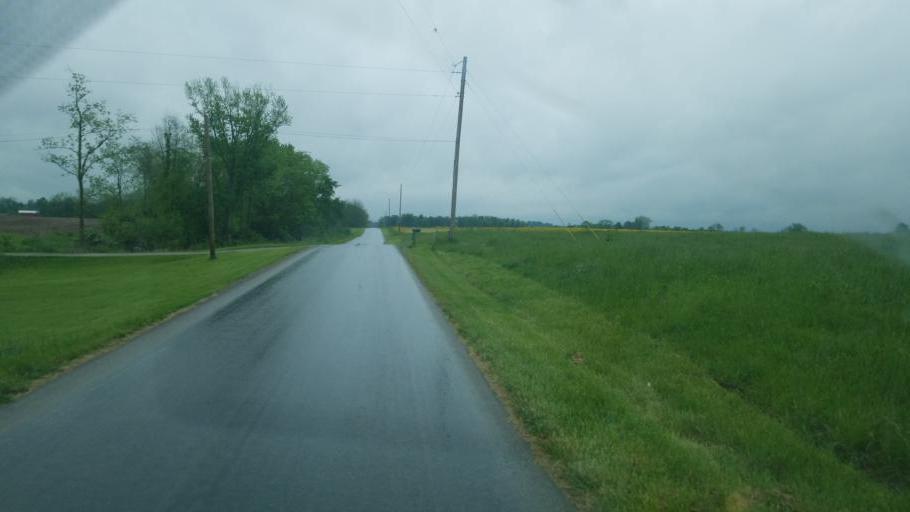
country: US
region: Ohio
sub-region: Highland County
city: Greenfield
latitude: 39.3260
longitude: -83.4267
